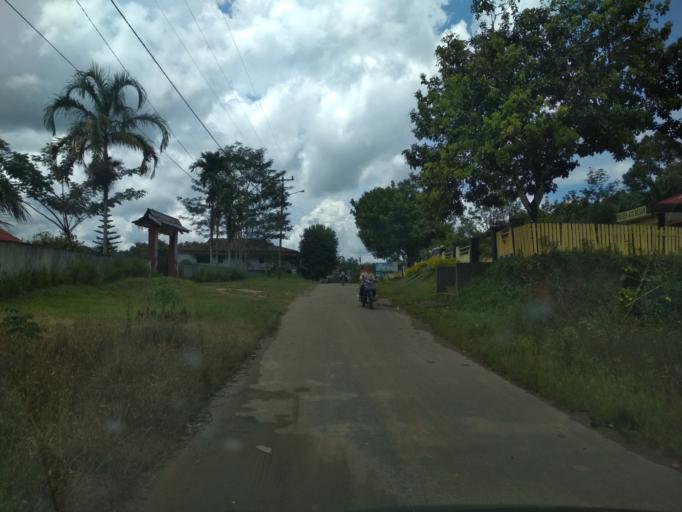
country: ID
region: West Kalimantan
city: Bengkayang
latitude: 0.7474
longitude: 110.1086
